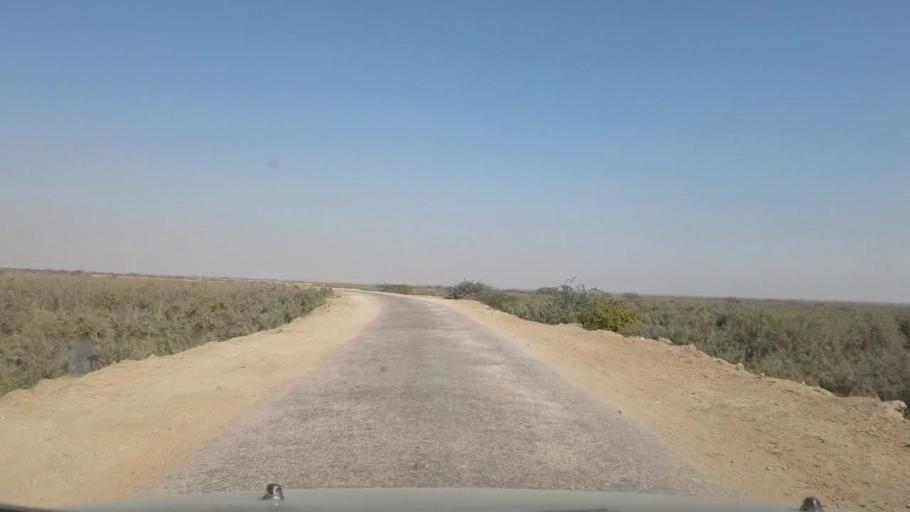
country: PK
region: Sindh
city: Thatta
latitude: 24.8231
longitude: 67.8927
